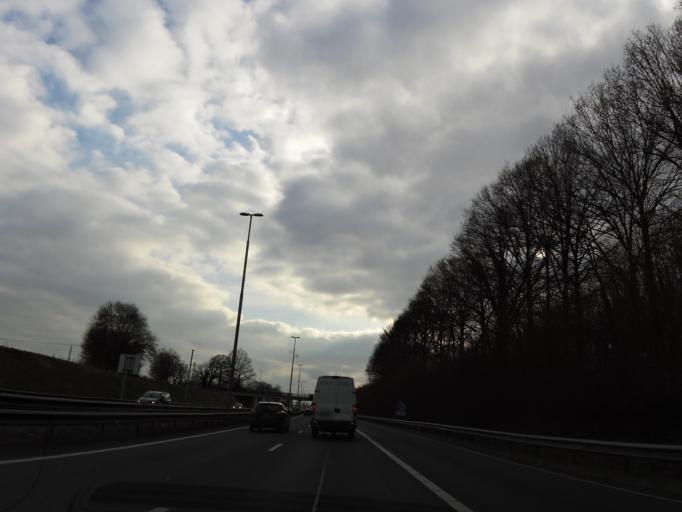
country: NL
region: Limburg
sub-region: Gemeente Stein
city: Berg
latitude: 51.0026
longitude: 5.7906
